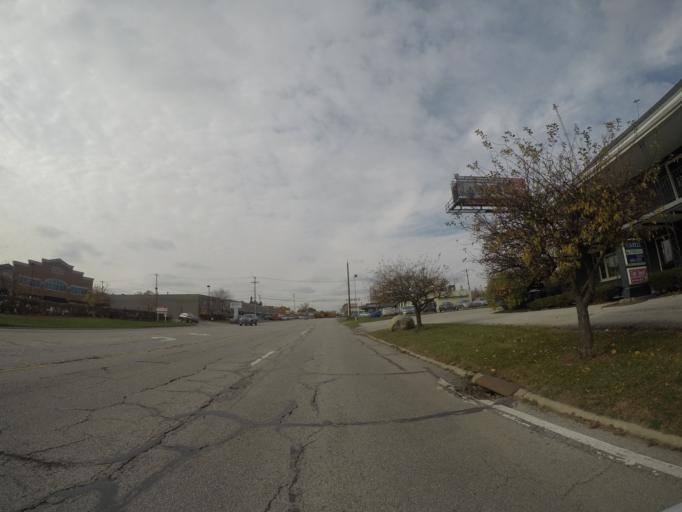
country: US
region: Ohio
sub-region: Franklin County
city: Upper Arlington
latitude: 40.0071
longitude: -83.0450
